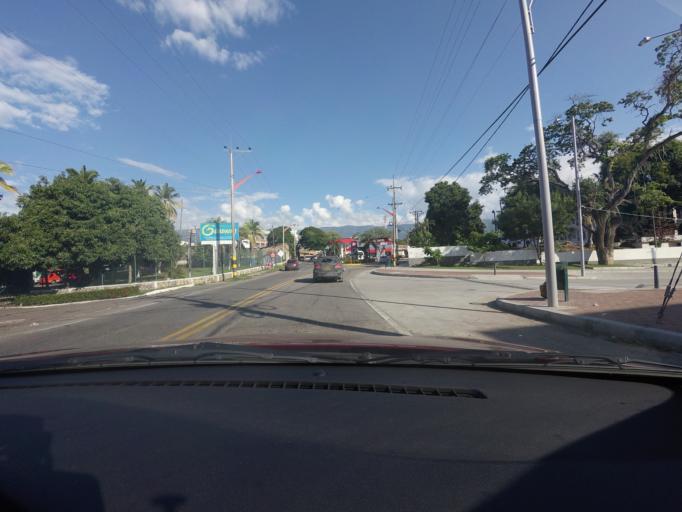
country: CO
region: Tolima
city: Melgar
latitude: 4.2055
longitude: -74.6452
